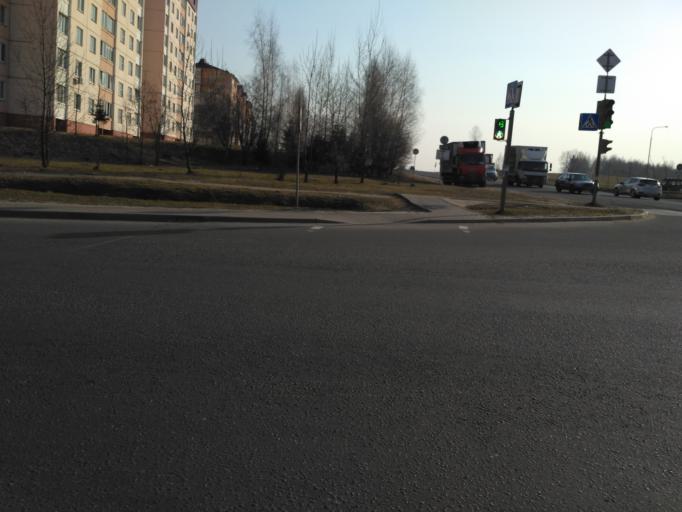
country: BY
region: Minsk
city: Zaslawye
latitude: 54.0144
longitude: 27.2580
